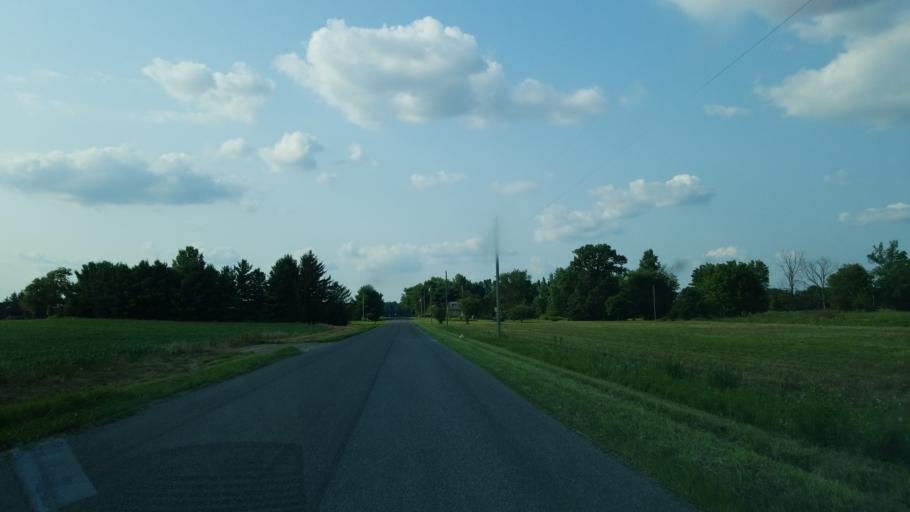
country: US
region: Ohio
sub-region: Union County
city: Marysville
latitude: 40.3111
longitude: -83.2928
